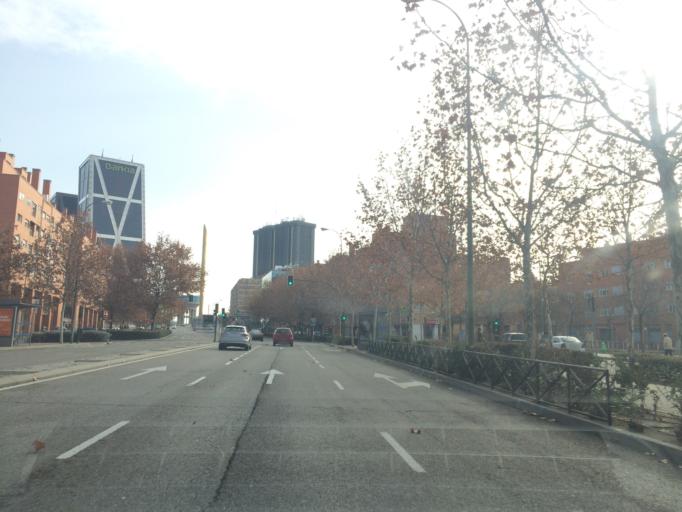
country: ES
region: Madrid
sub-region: Provincia de Madrid
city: Chamartin
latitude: 40.4688
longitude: -3.6947
